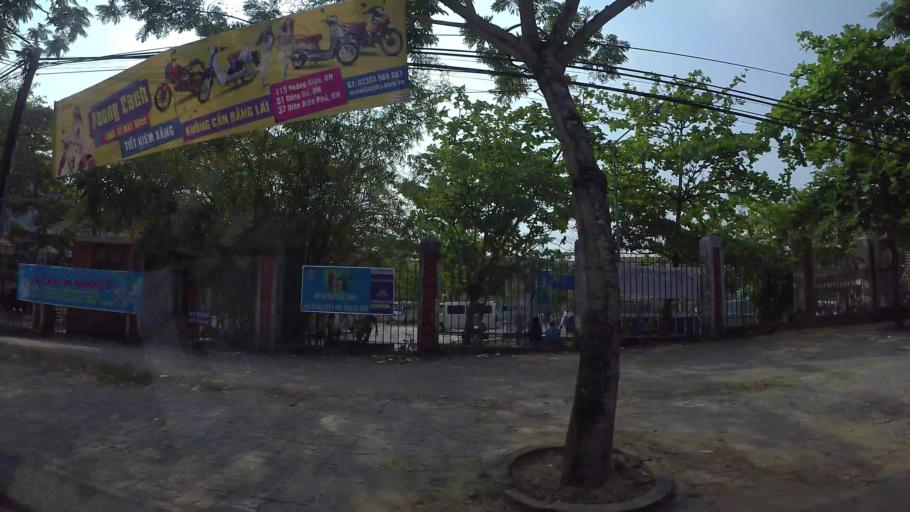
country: VN
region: Da Nang
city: Ngu Hanh Son
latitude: 16.0299
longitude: 108.2459
